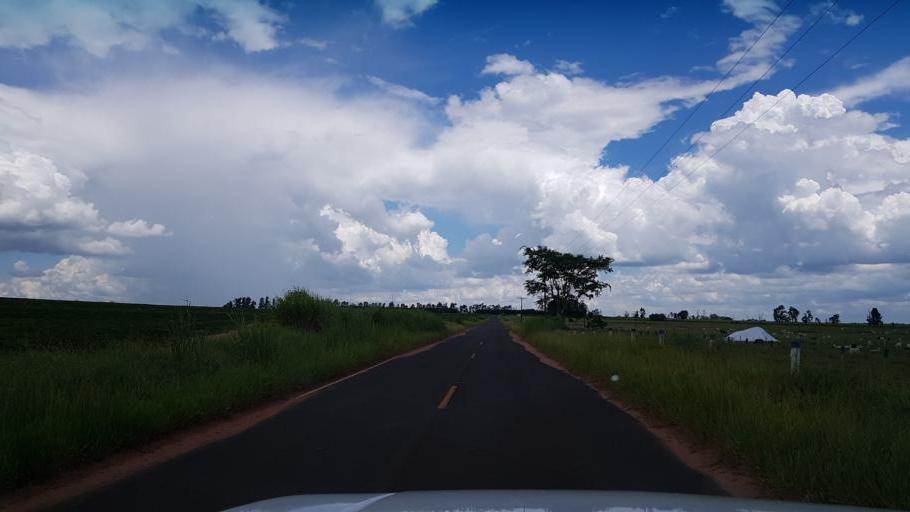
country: BR
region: Sao Paulo
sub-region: Paraguacu Paulista
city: Paraguacu Paulista
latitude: -22.3590
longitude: -50.6268
